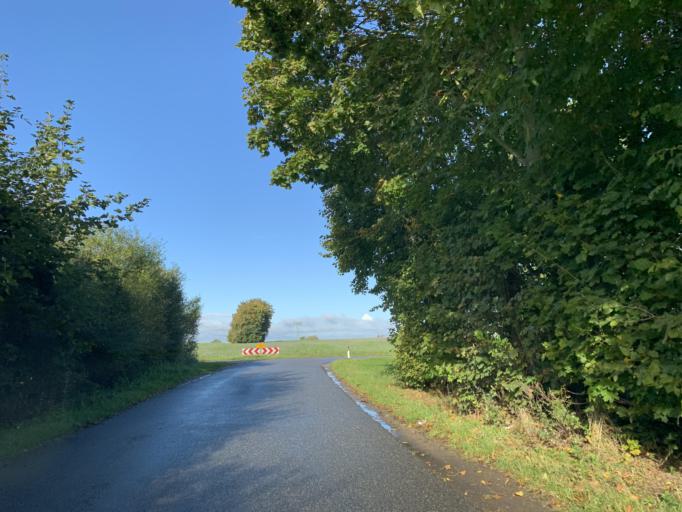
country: DE
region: Mecklenburg-Vorpommern
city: Gross Nemerow
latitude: 53.4736
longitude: 13.2653
